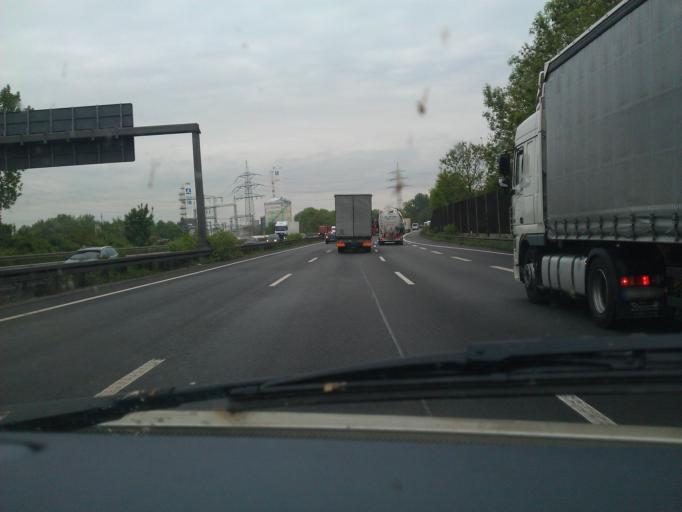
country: DE
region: North Rhine-Westphalia
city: Meiderich
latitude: 51.5163
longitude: 6.8157
